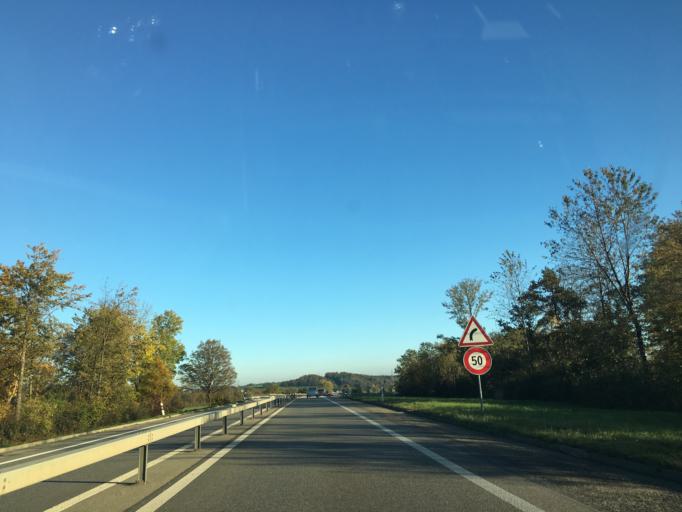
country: CH
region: Solothurn
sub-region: Bezirk Gaeu
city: Oensingen
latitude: 47.2843
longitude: 7.7228
